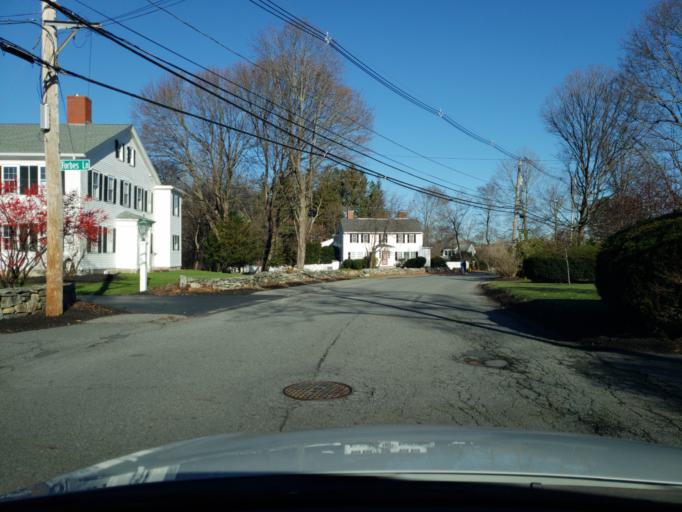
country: US
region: Massachusetts
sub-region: Essex County
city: Andover
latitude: 42.6409
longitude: -71.1330
